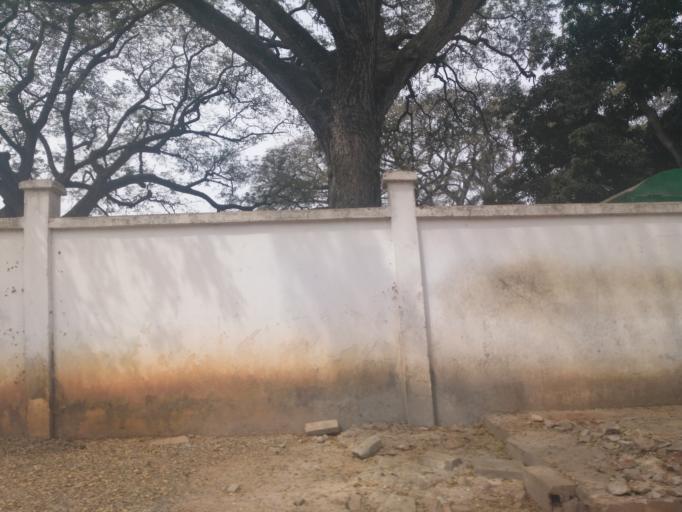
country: GH
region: Ashanti
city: Kumasi
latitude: 6.6714
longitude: -1.6172
